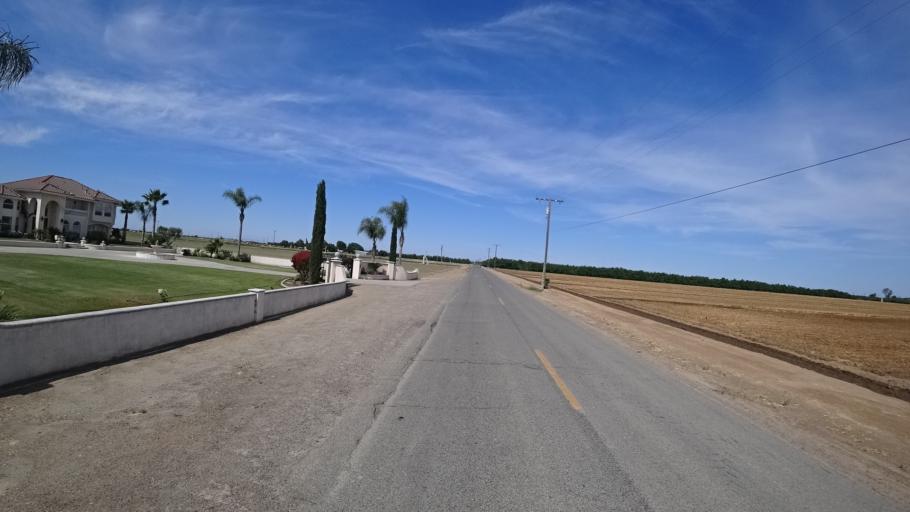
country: US
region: California
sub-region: Kings County
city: Hanford
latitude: 36.3573
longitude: -119.5763
